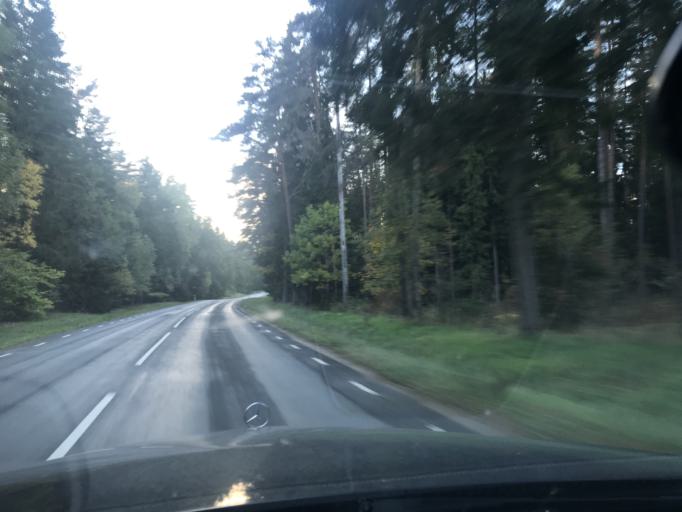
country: EE
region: Vorumaa
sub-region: Antsla vald
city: Vana-Antsla
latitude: 57.8799
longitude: 26.7618
